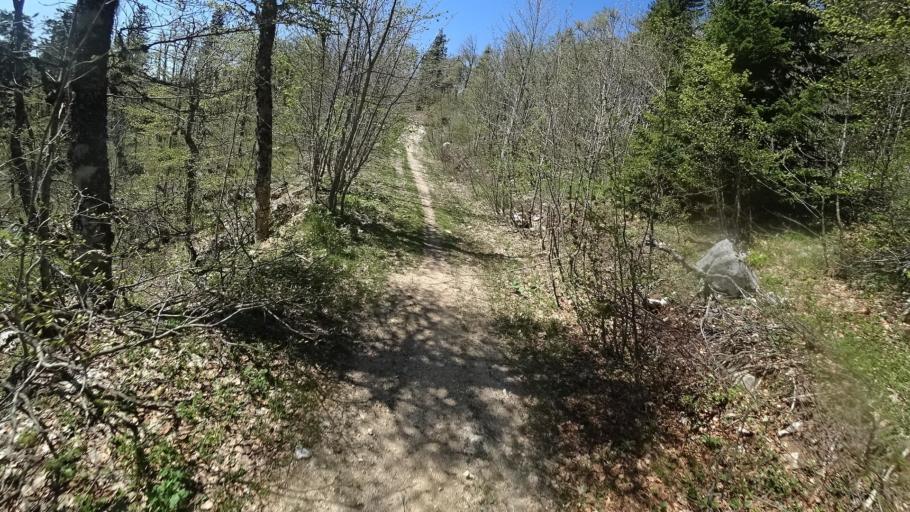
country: BA
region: Federation of Bosnia and Herzegovina
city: Rumboci
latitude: 43.8728
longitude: 17.4654
